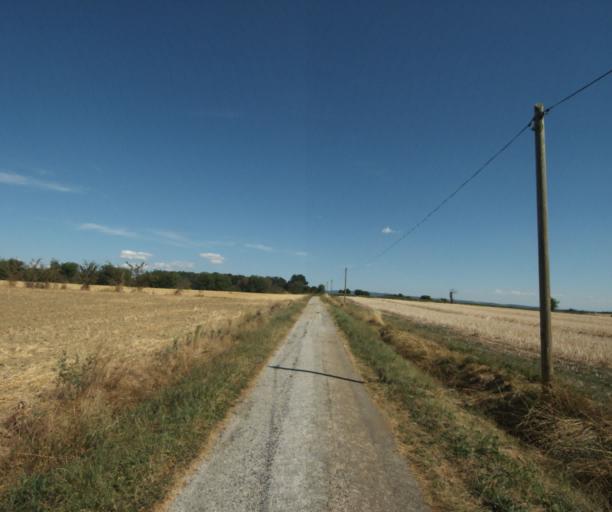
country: FR
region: Midi-Pyrenees
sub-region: Departement de la Haute-Garonne
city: Saint-Felix-Lauragais
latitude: 43.5069
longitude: 1.9077
